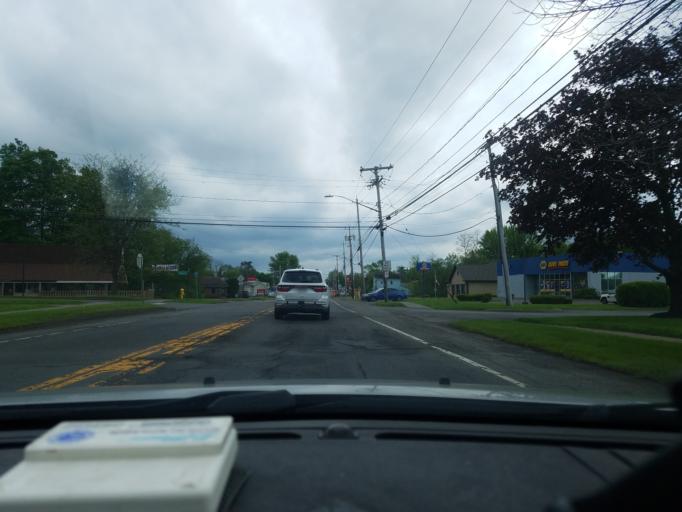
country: US
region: New York
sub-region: Onondaga County
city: North Syracuse
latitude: 43.1433
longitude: -76.1273
